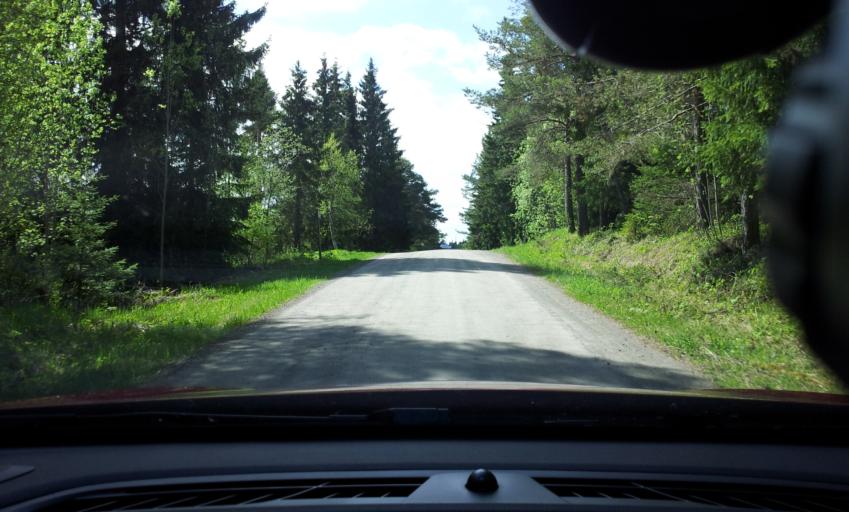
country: SE
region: Jaemtland
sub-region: Bergs Kommun
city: Hoverberg
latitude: 62.9457
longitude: 14.5227
